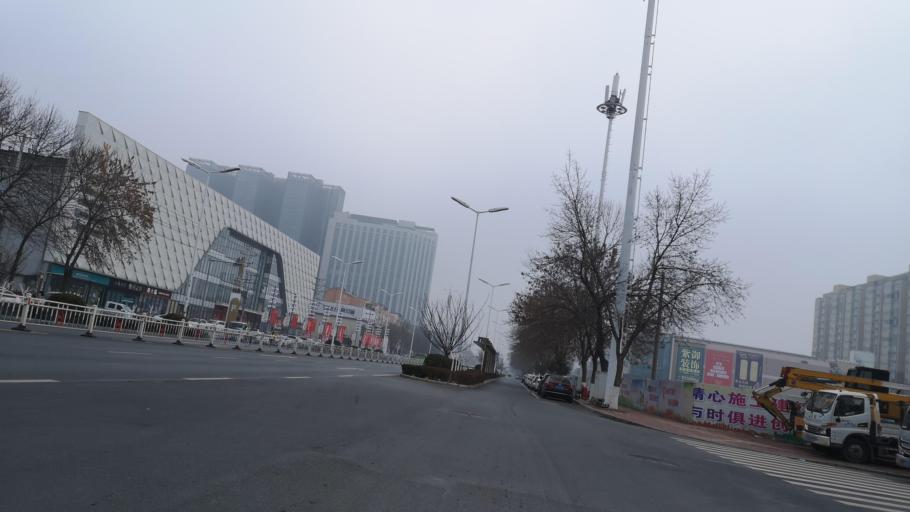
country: CN
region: Henan Sheng
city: Zhongyuanlu
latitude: 35.7711
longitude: 115.0545
